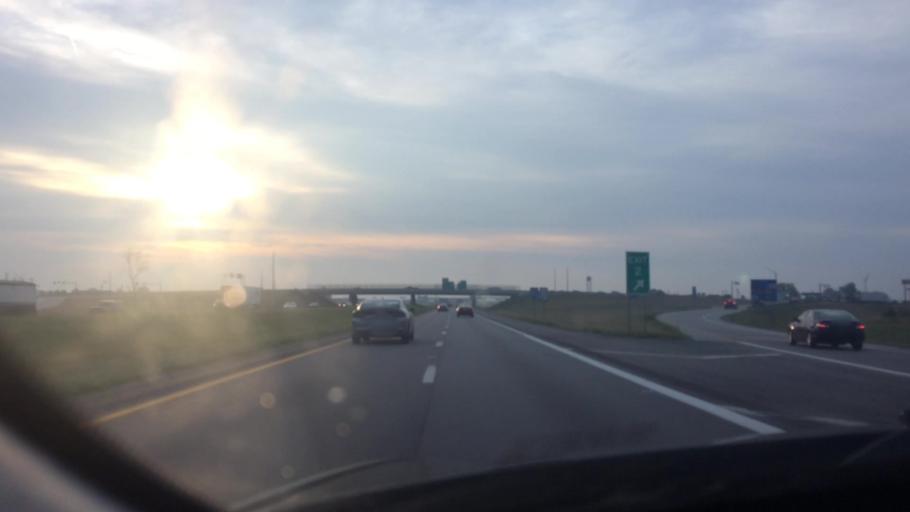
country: US
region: Ohio
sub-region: Wood County
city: Perrysburg
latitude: 41.5323
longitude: -83.6409
